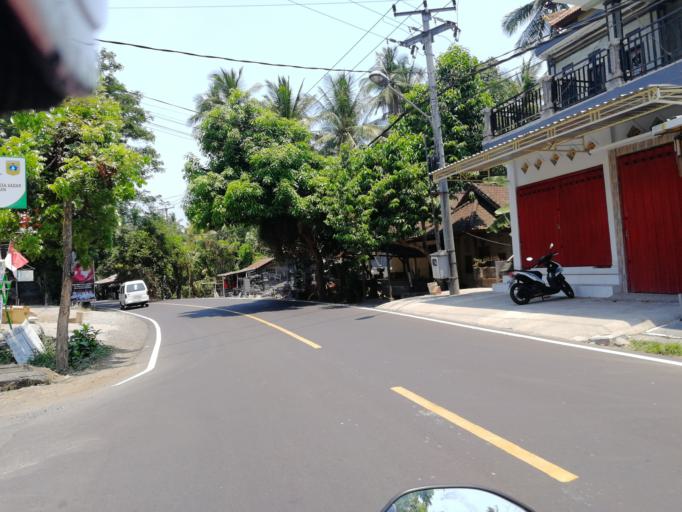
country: ID
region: Bali
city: Banjar Kawan
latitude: -8.4994
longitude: 115.5469
